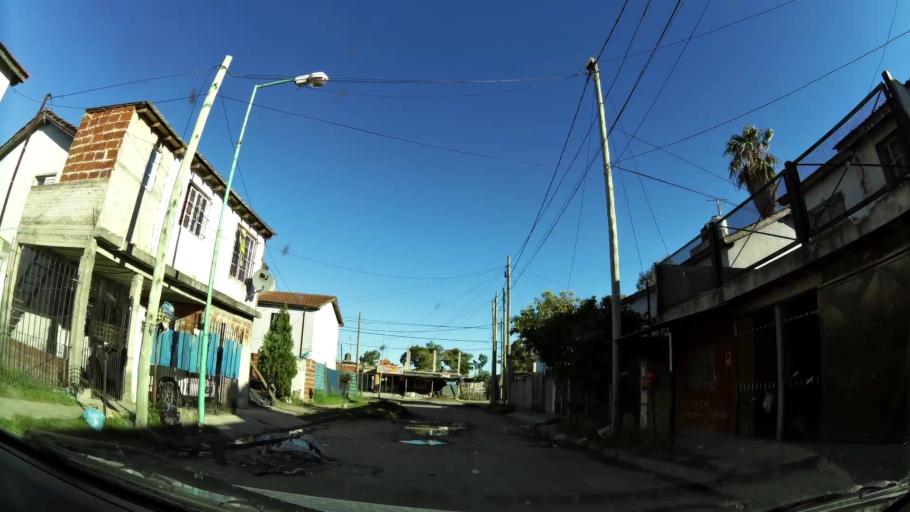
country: AR
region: Buenos Aires
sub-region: Partido de Lanus
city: Lanus
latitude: -34.7437
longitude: -58.3325
